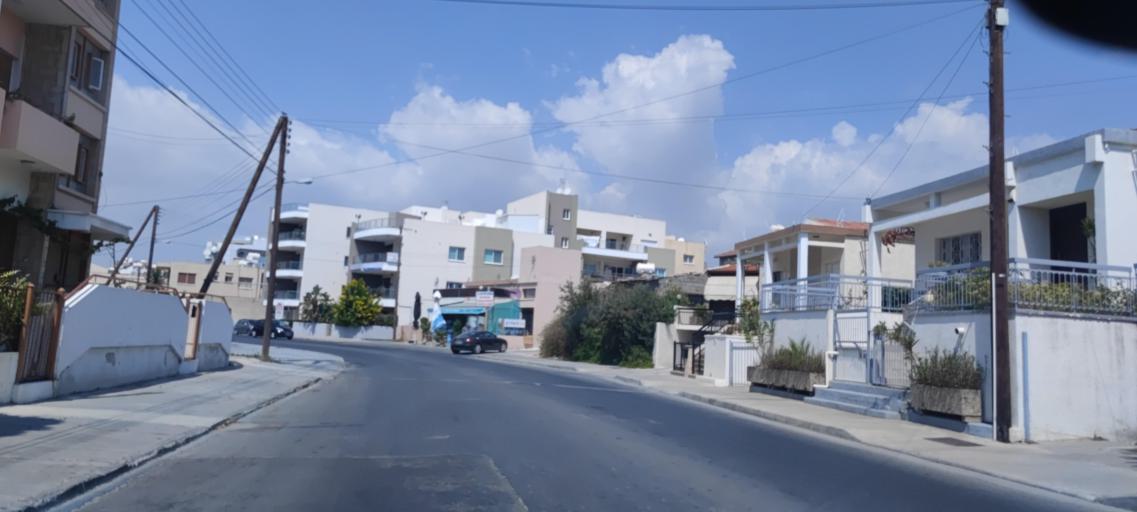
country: CY
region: Limassol
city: Limassol
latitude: 34.6906
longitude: 33.0319
